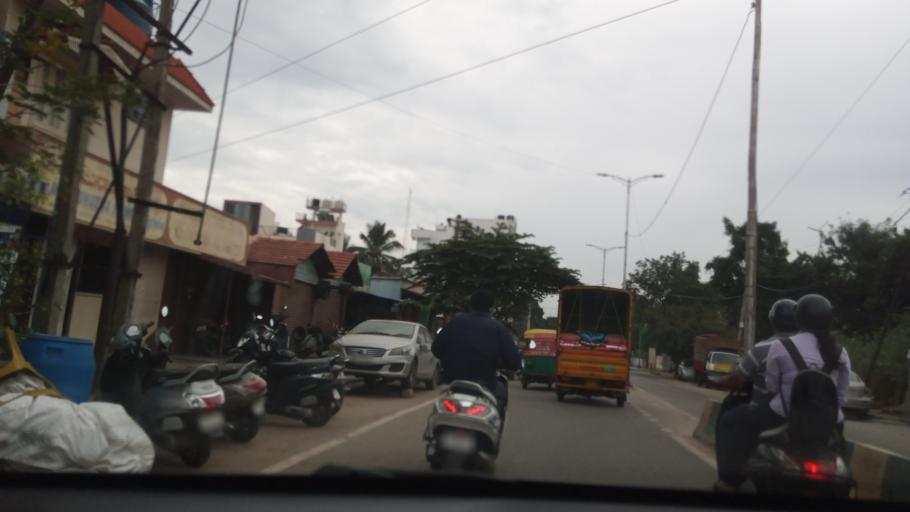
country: IN
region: Karnataka
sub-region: Bangalore Urban
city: Bangalore
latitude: 13.0157
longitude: 77.5393
